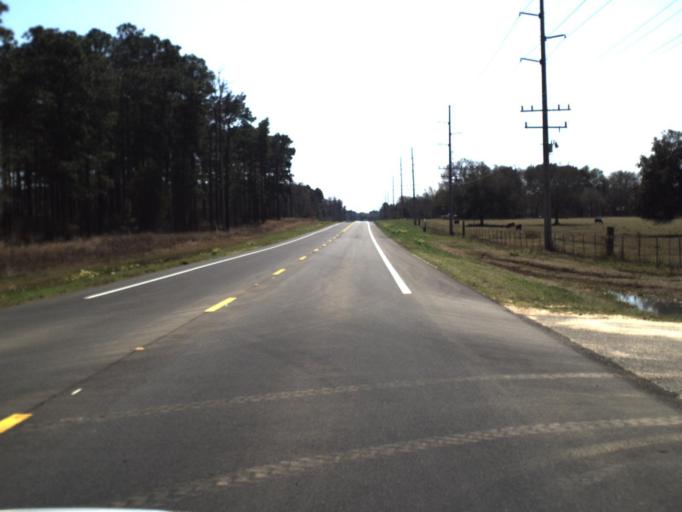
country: US
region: Florida
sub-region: Jackson County
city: Sneads
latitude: 30.7521
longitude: -85.0195
